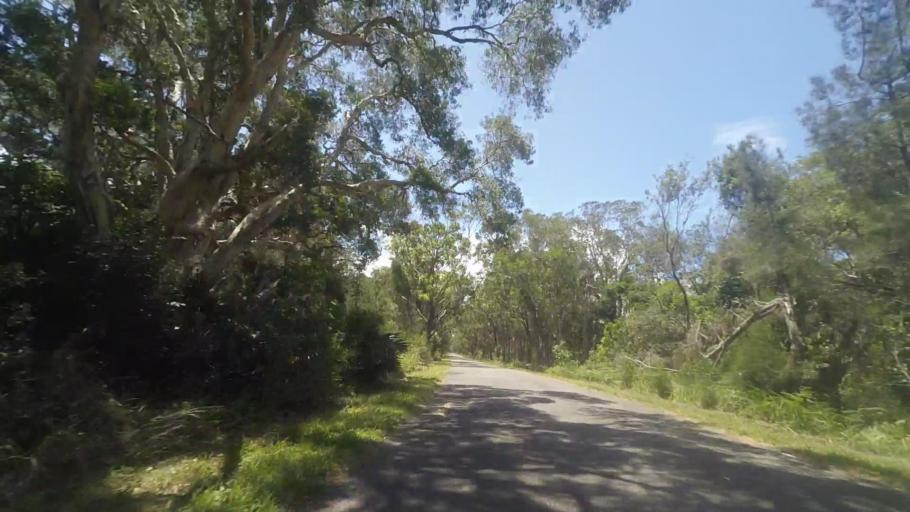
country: AU
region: New South Wales
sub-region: Great Lakes
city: Bulahdelah
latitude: -32.5296
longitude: 152.3228
